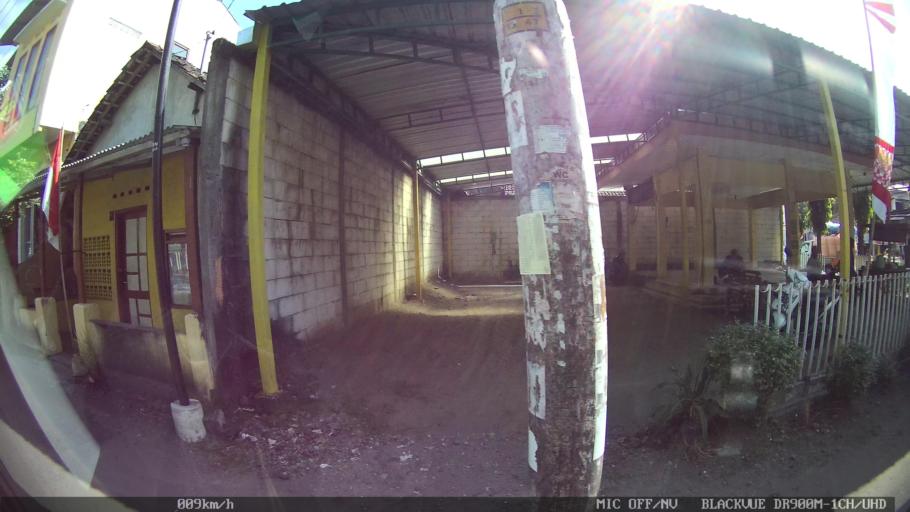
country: ID
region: Daerah Istimewa Yogyakarta
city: Yogyakarta
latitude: -7.8226
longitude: 110.3727
